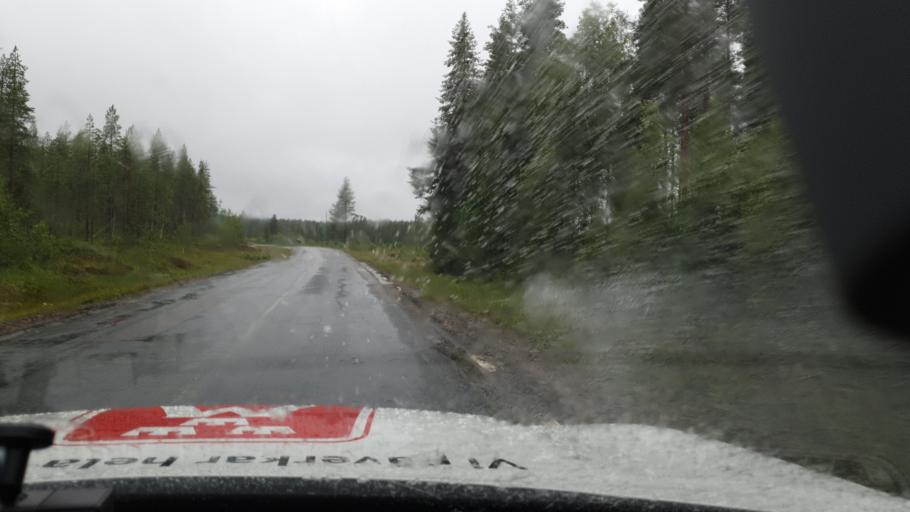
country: SE
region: Vaesterbotten
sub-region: Skelleftea Kommun
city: Boliden
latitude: 65.0343
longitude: 20.3220
